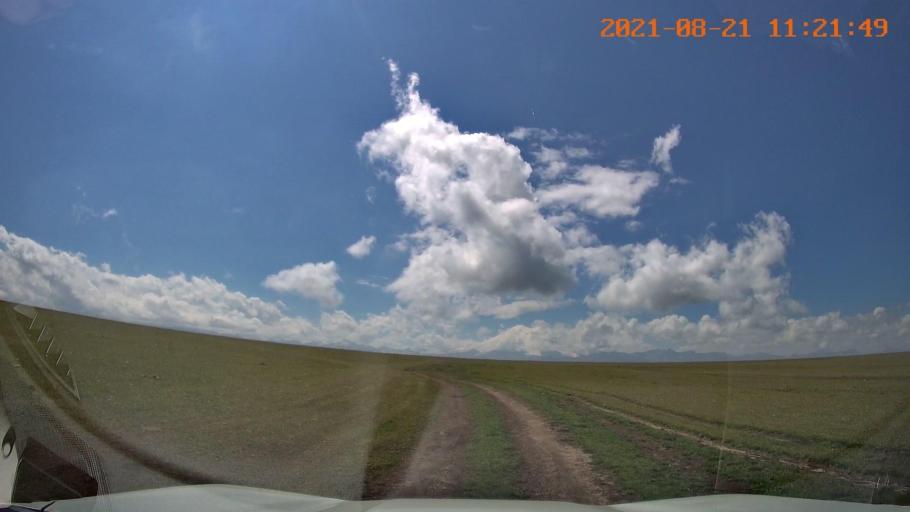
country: RU
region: Stavropol'skiy
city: Kislovodsk
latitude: 43.6170
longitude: 42.5923
